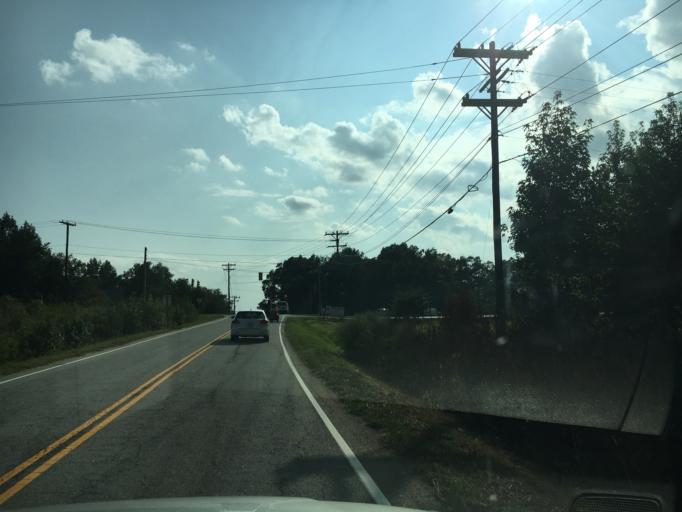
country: US
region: South Carolina
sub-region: Greenville County
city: Wade Hampton
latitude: 34.9400
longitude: -82.3334
